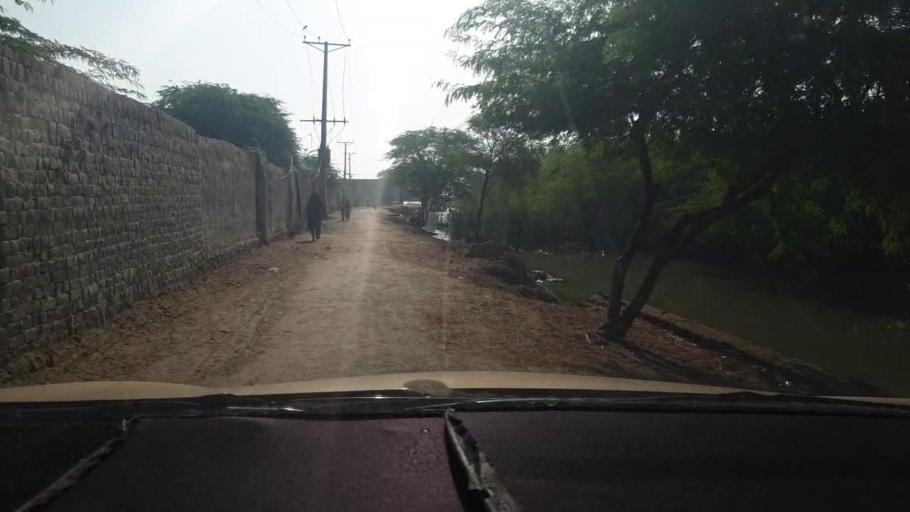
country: PK
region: Sindh
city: Kambar
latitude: 27.5806
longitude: 68.0983
